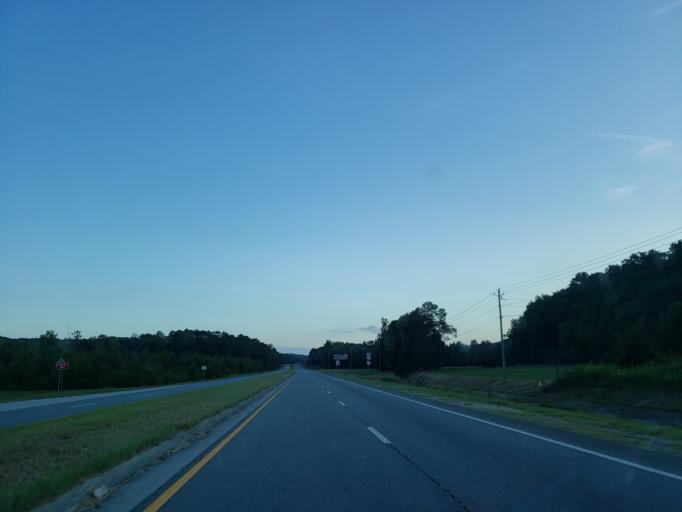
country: US
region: Georgia
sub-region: Floyd County
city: Lindale
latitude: 34.1629
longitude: -85.2132
